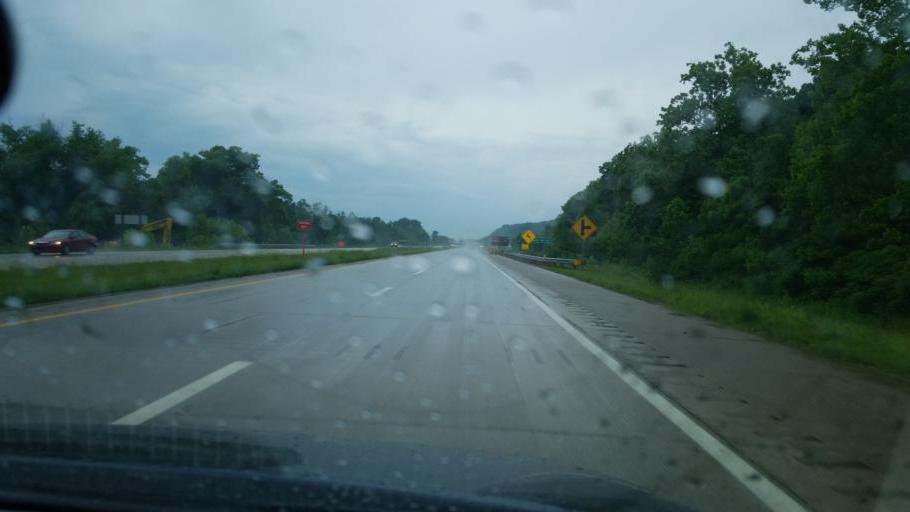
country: US
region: Ohio
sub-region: Athens County
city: Athens
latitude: 39.3344
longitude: -82.0167
